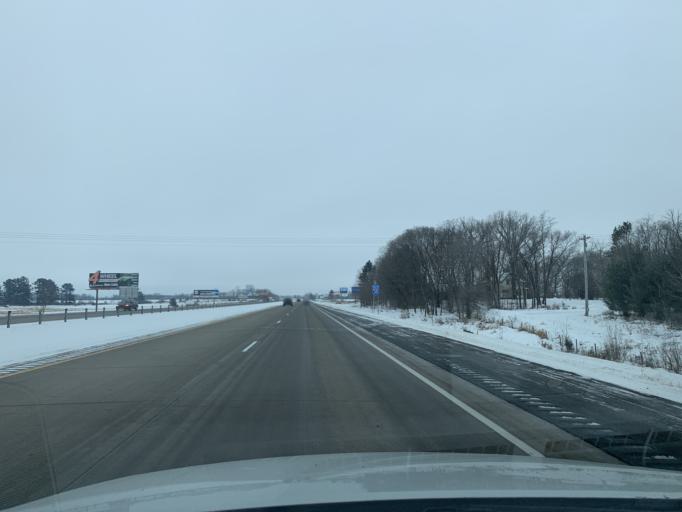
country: US
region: Minnesota
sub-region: Pine County
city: Rock Creek
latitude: 45.7603
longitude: -92.9905
